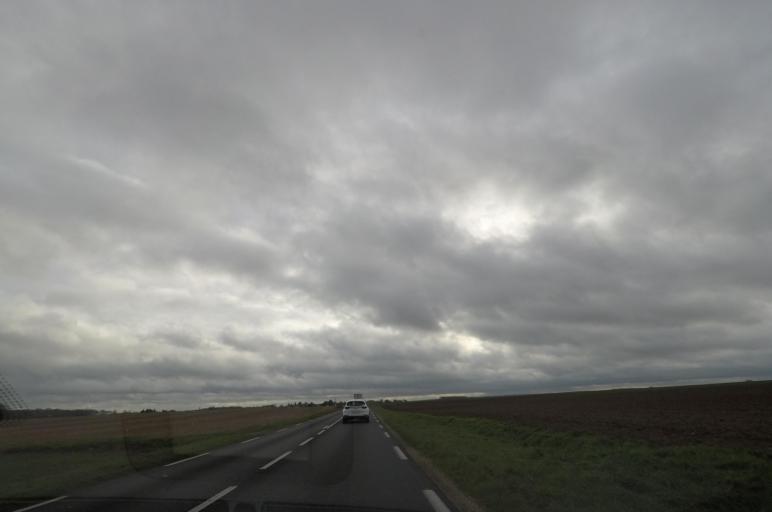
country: FR
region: Centre
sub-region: Departement du Loir-et-Cher
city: Herbault
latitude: 47.6976
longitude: 1.1819
